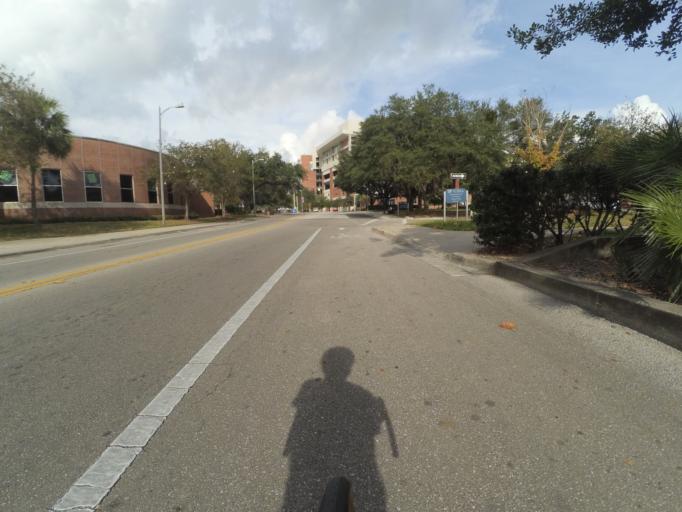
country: US
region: Florida
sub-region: Alachua County
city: Gainesville
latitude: 29.6477
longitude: -82.3497
